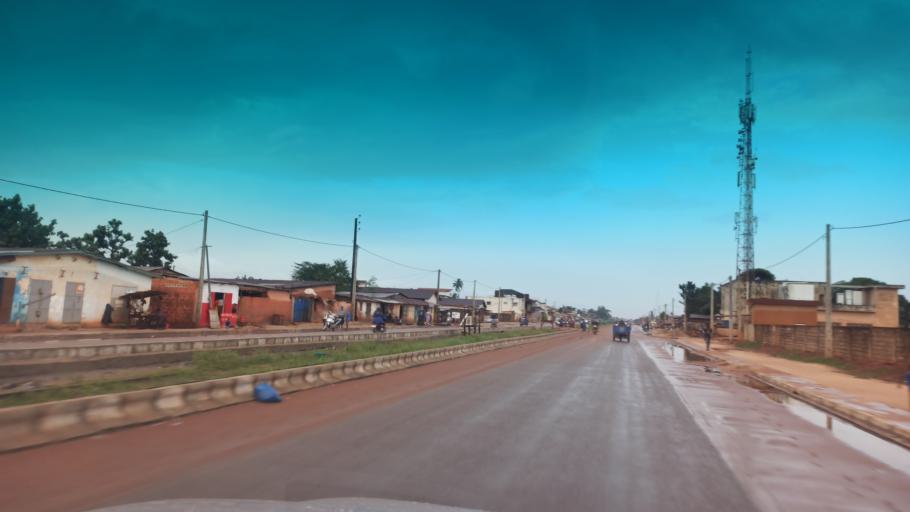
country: BJ
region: Queme
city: Porto-Novo
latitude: 6.4941
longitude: 2.6262
